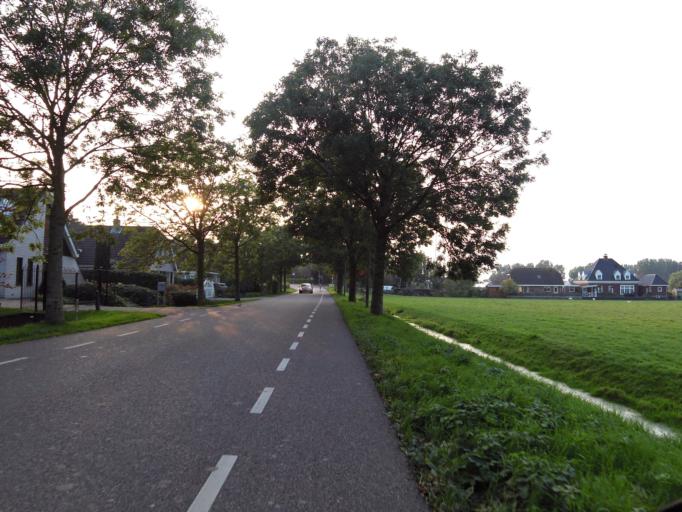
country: NL
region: South Holland
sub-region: Gemeente Rijnwoude
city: Benthuizen
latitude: 52.0782
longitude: 4.5566
